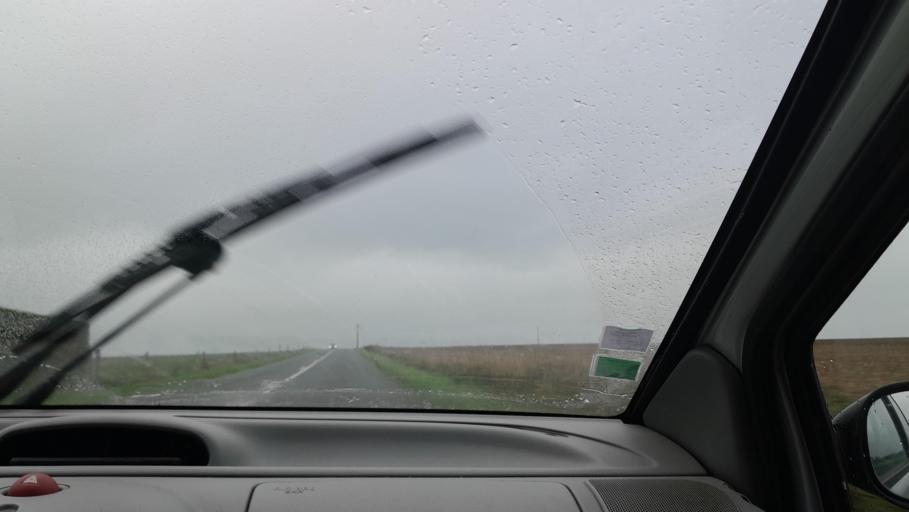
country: FR
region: Pays de la Loire
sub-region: Departement de la Mayenne
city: Congrier
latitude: 47.8550
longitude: -1.1341
